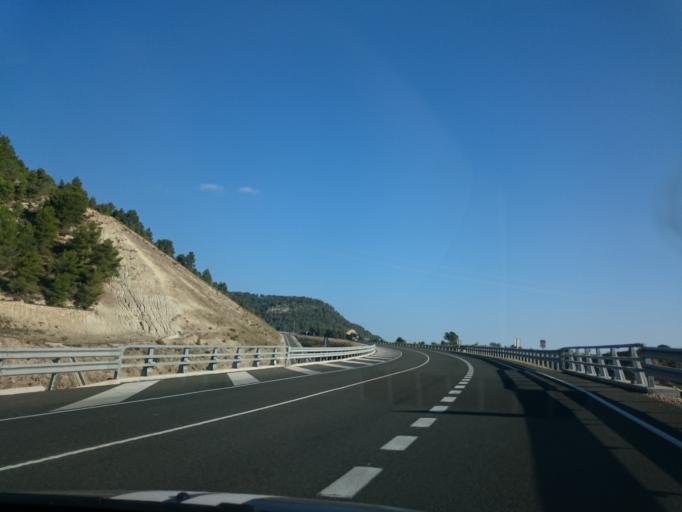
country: ES
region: Catalonia
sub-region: Provincia de Barcelona
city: Odena
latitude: 41.6012
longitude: 1.6740
